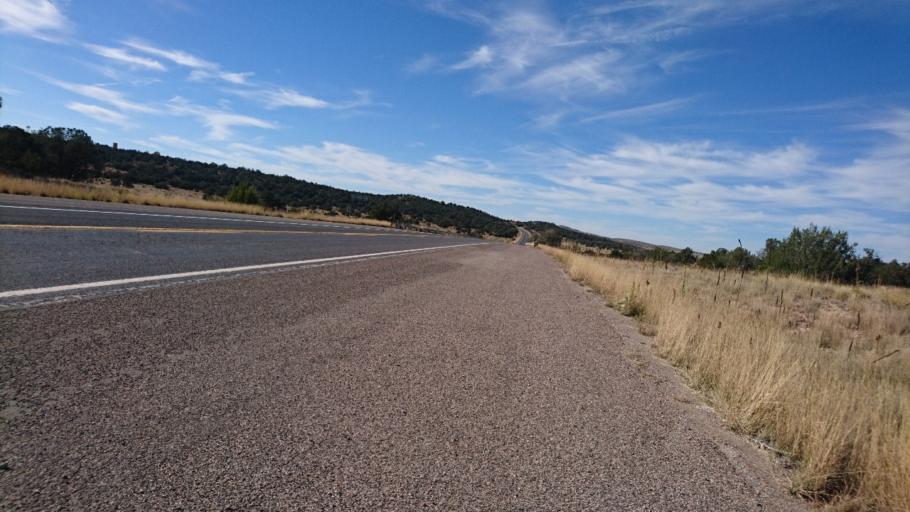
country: US
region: Arizona
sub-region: Mohave County
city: Peach Springs
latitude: 35.5203
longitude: -113.2052
